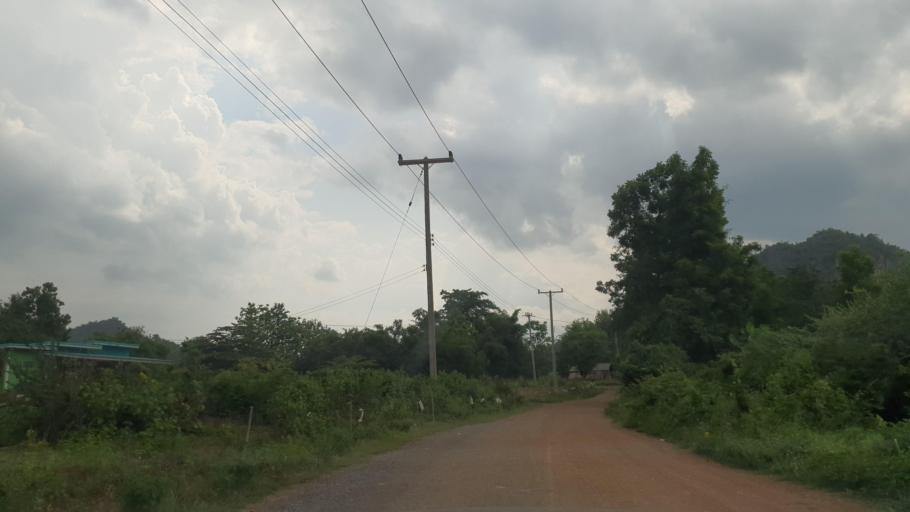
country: TH
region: Sukhothai
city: Thung Saliam
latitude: 17.2503
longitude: 99.5459
